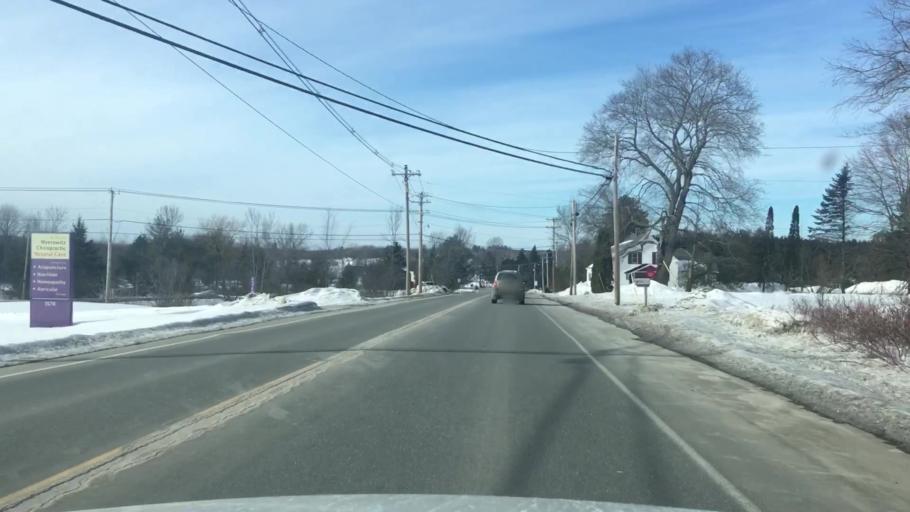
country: US
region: Maine
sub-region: Penobscot County
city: Bangor
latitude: 44.8489
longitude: -68.8036
